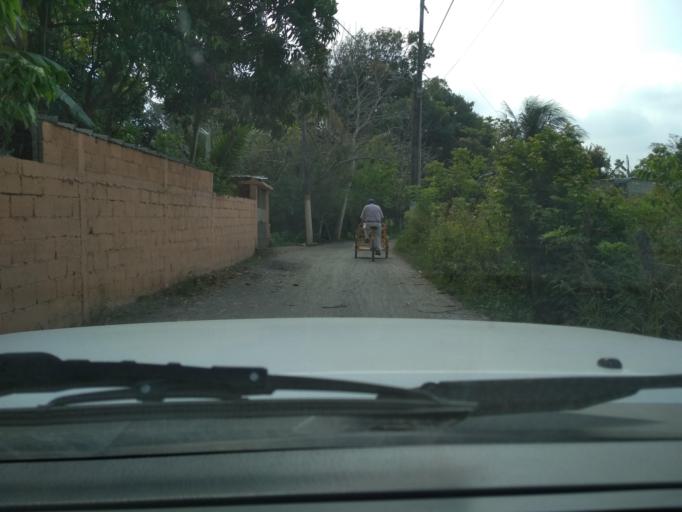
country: MX
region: Veracruz
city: El Tejar
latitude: 19.0816
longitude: -96.1655
